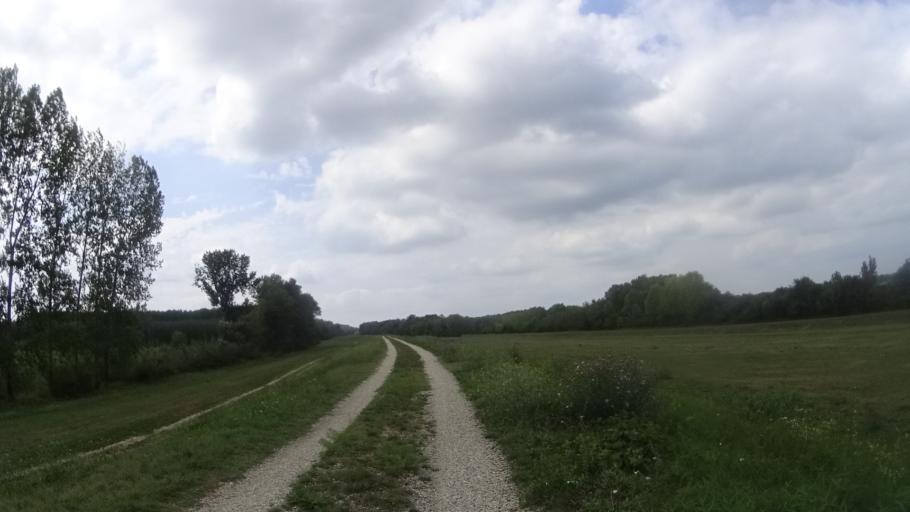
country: SK
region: Trnavsky
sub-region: Okres Dunajska Streda
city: Velky Meder
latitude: 47.7558
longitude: 17.7586
